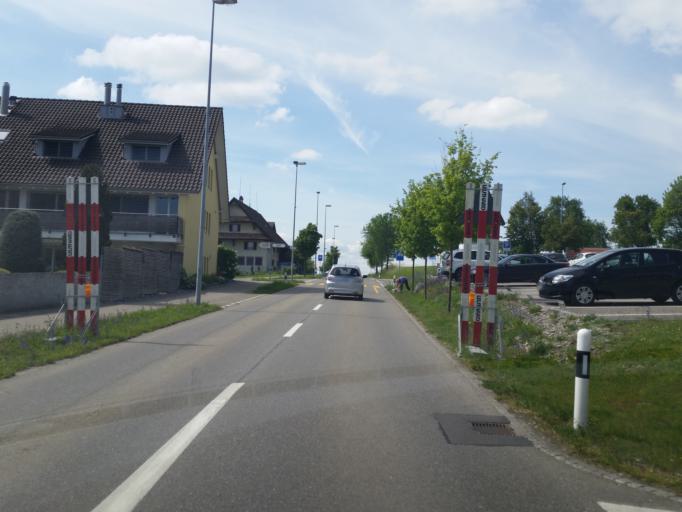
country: CH
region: Aargau
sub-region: Bezirk Bremgarten
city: Unterlunkhofen
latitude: 47.3365
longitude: 8.3866
